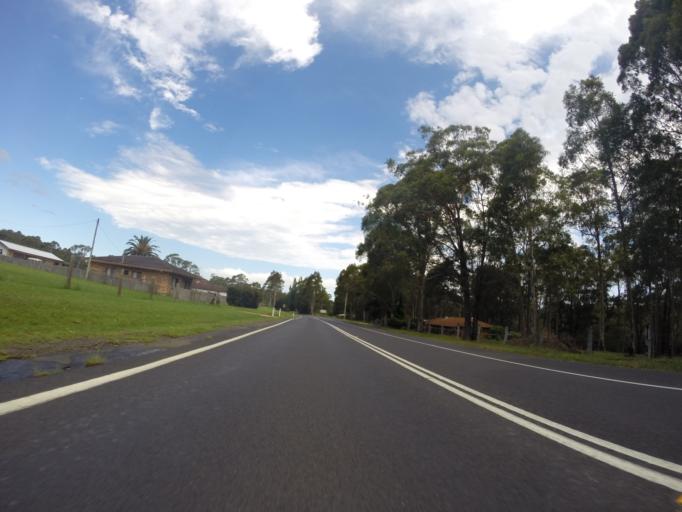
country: AU
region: New South Wales
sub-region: Shoalhaven Shire
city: Falls Creek
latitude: -35.0826
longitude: 150.5280
